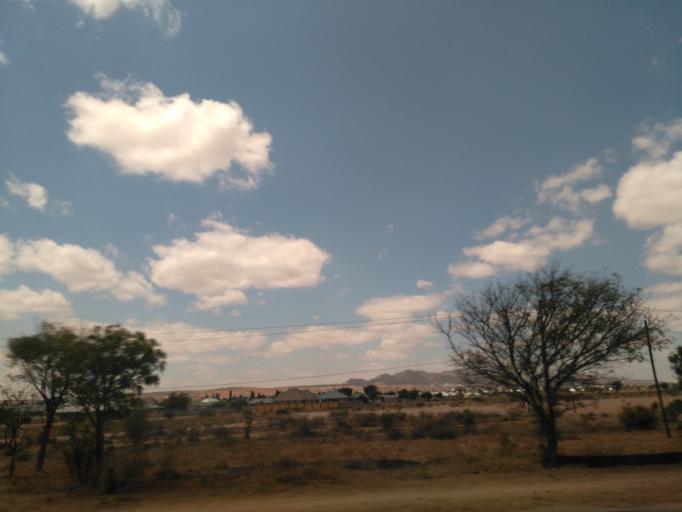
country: TZ
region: Dodoma
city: Kisasa
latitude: -6.1668
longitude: 35.7824
